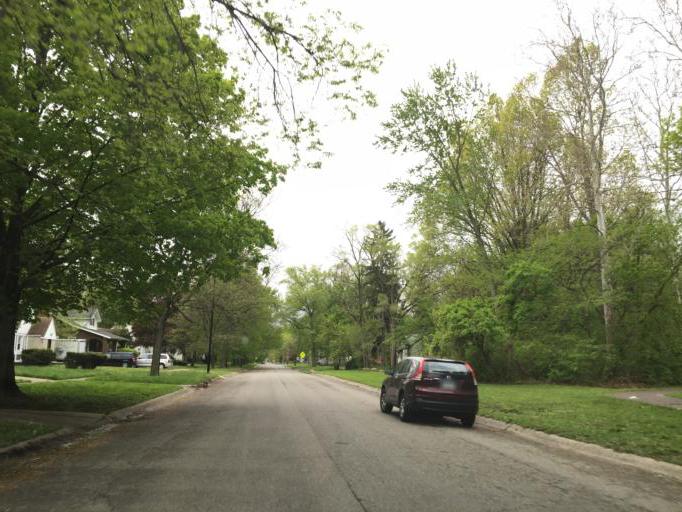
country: US
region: Michigan
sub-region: Wayne County
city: Redford
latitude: 42.3956
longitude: -83.2323
